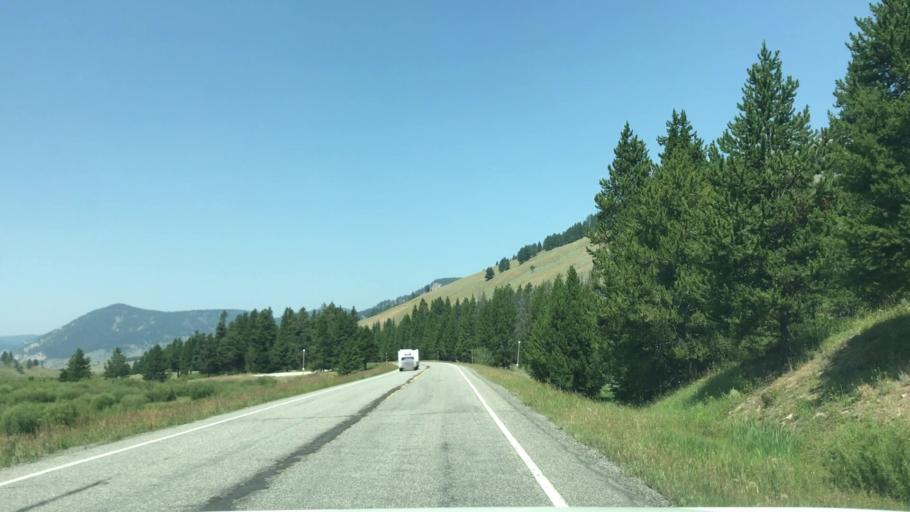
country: US
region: Montana
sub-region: Gallatin County
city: Big Sky
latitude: 45.0324
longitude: -111.1118
